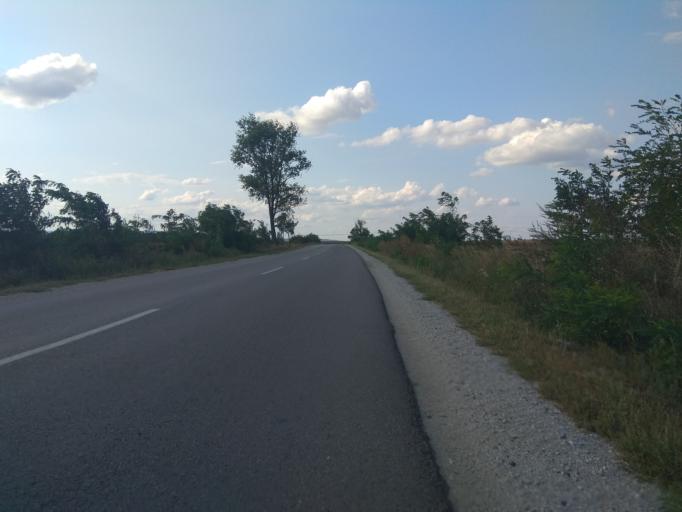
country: HU
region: Borsod-Abauj-Zemplen
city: Hejobaba
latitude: 47.9034
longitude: 20.8891
